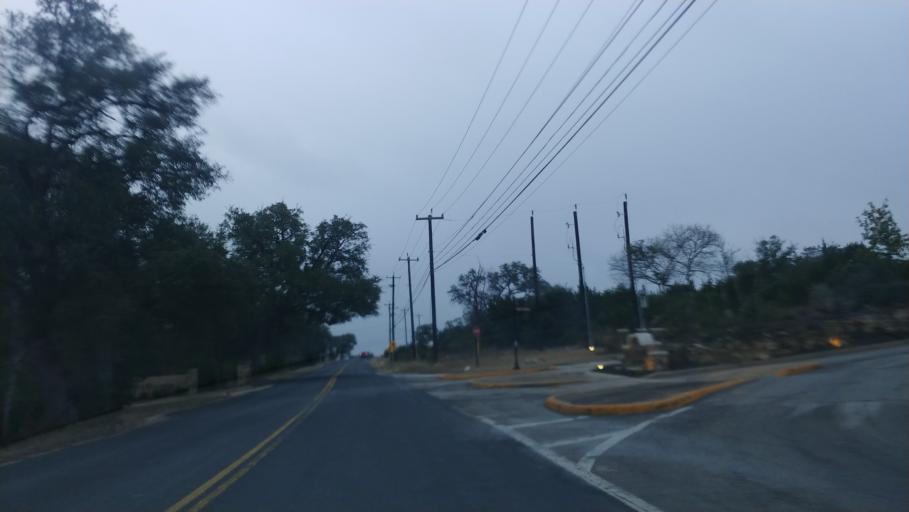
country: US
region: Texas
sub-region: Bexar County
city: Cross Mountain
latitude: 29.6618
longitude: -98.6776
